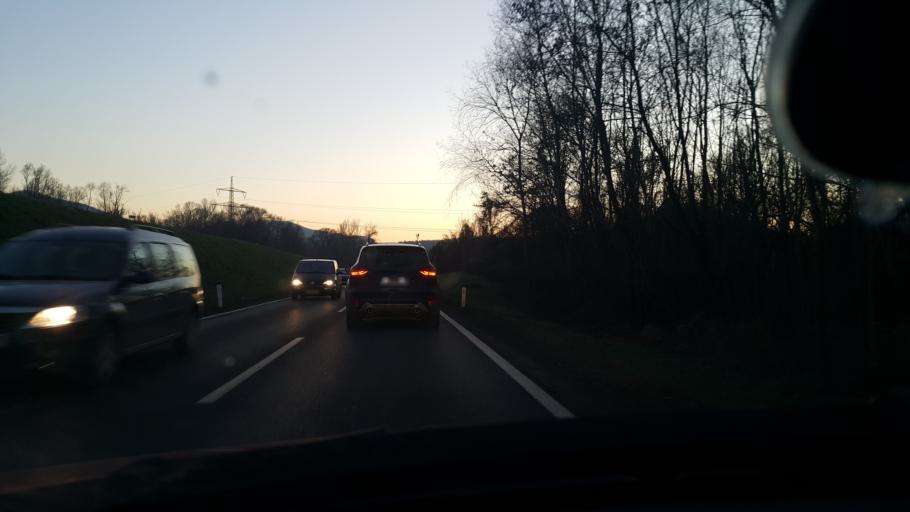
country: AT
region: Styria
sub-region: Politischer Bezirk Graz-Umgebung
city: Gratwein
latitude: 47.1360
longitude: 15.3269
